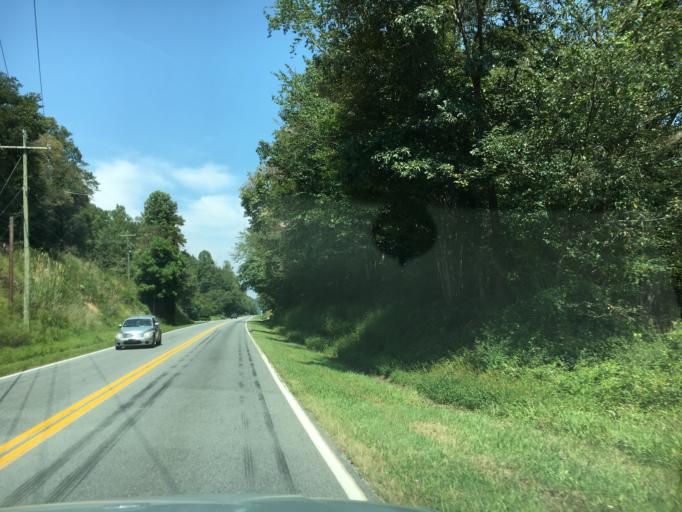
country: US
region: North Carolina
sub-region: McDowell County
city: West Marion
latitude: 35.6261
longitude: -81.9865
